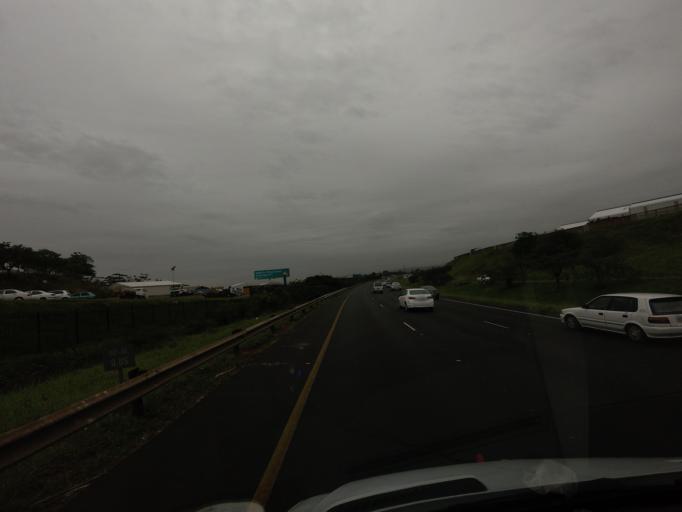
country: ZA
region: KwaZulu-Natal
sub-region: eThekwini Metropolitan Municipality
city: Durban
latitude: -29.7476
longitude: 31.0355
